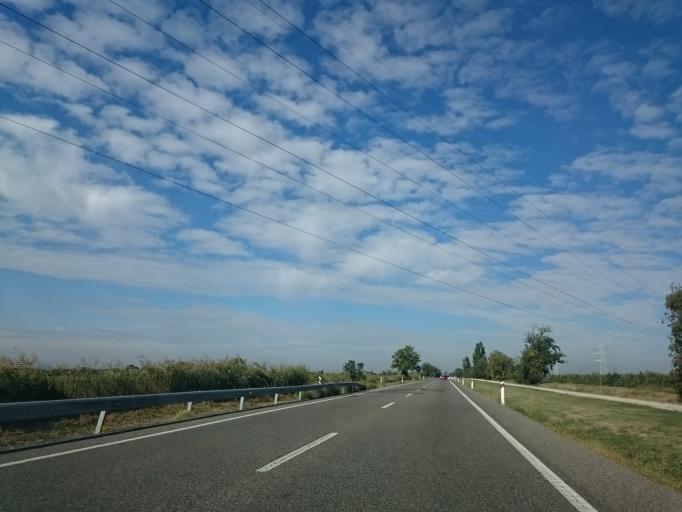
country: ES
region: Catalonia
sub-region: Provincia de Lleida
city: Juneda
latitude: 41.5793
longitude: 0.7499
